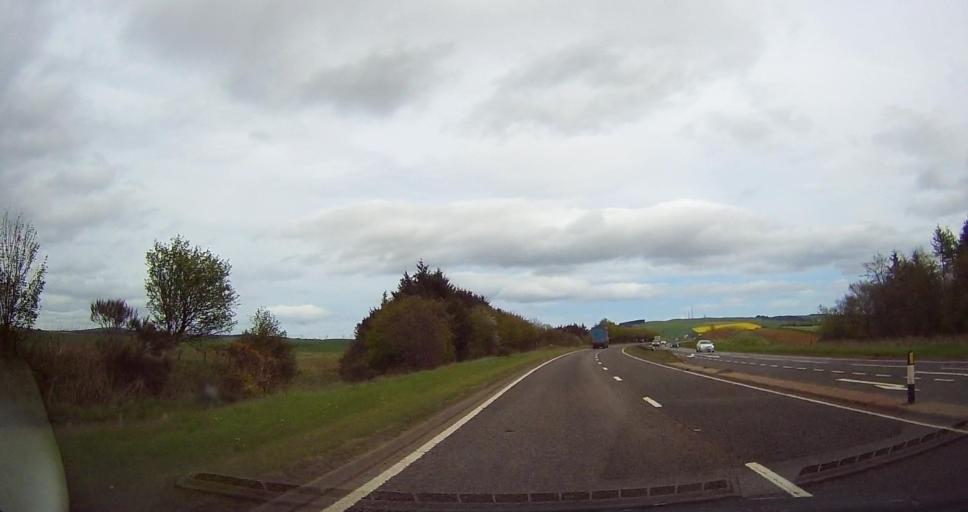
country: GB
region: Scotland
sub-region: Aberdeenshire
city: Inverbervie
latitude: 56.9095
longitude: -2.3539
